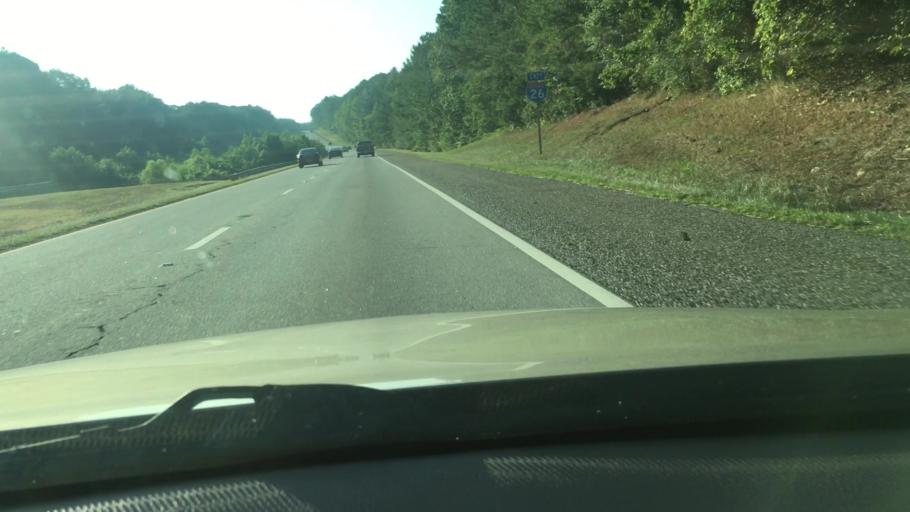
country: US
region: South Carolina
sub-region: Lexington County
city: Chapin
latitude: 34.1739
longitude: -81.3146
